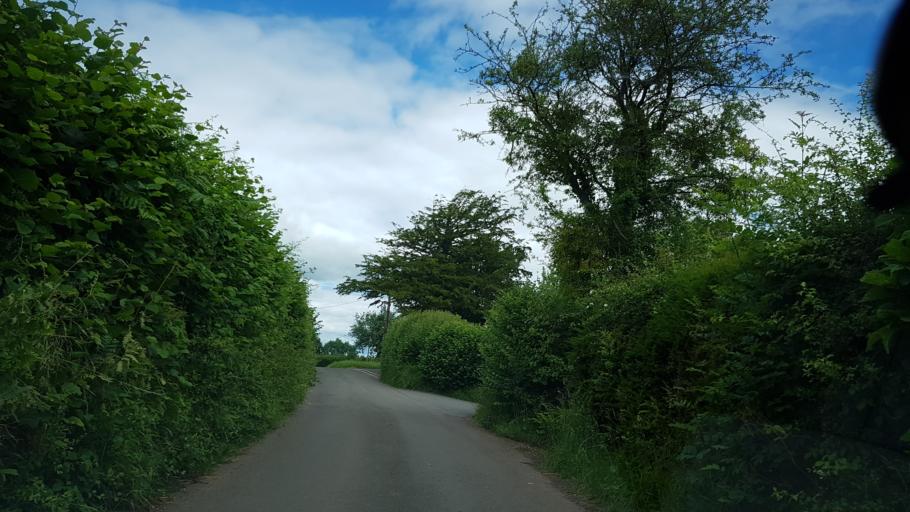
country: GB
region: Wales
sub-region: Monmouthshire
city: Llanarth
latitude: 51.7976
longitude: -2.8251
